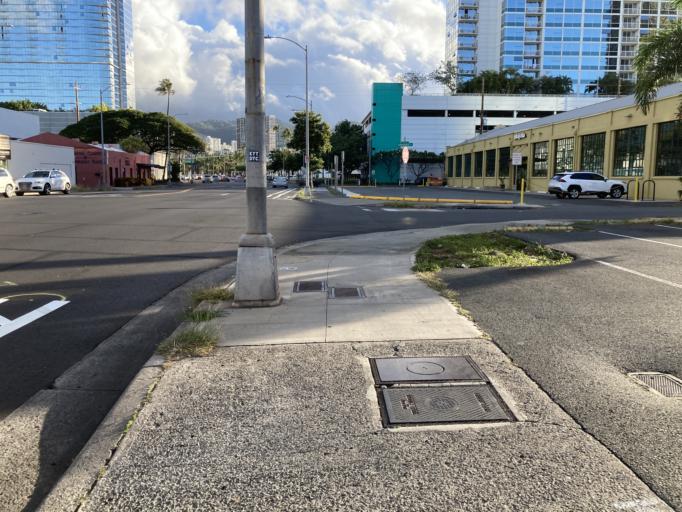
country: US
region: Hawaii
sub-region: Honolulu County
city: Honolulu
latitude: 21.2978
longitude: -157.8539
